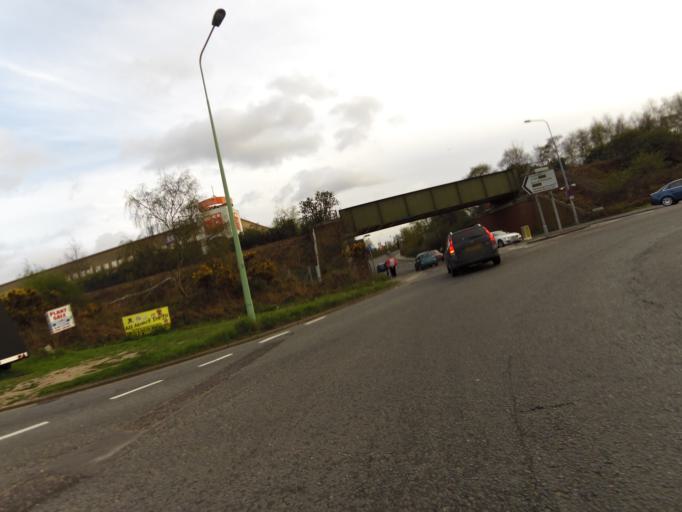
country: GB
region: England
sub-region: Suffolk
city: Kesgrave
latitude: 52.0357
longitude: 1.2078
